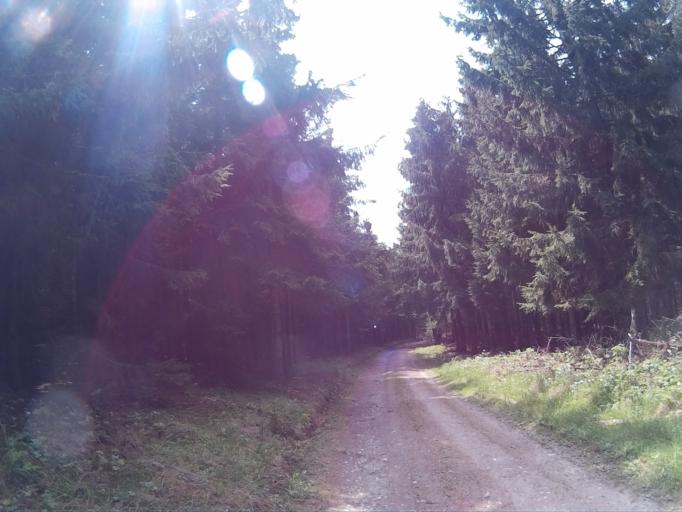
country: AT
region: Burgenland
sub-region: Politischer Bezirk Oberwart
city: Rechnitz
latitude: 47.3605
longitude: 16.4681
